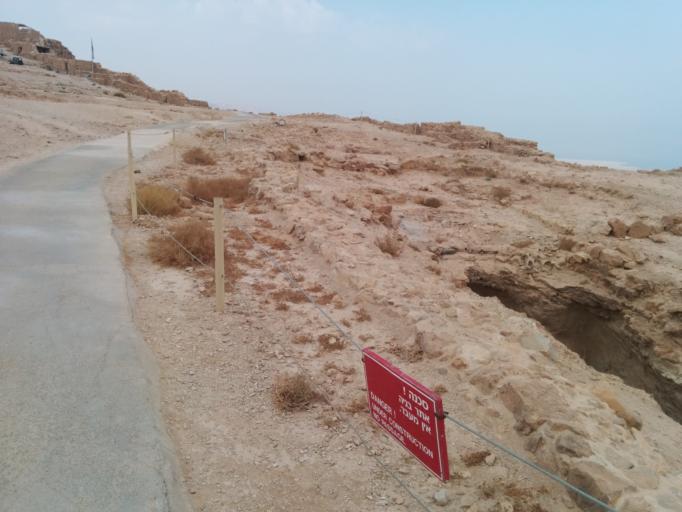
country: IL
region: Southern District
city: `En Boqeq
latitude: 31.3152
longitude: 35.3550
